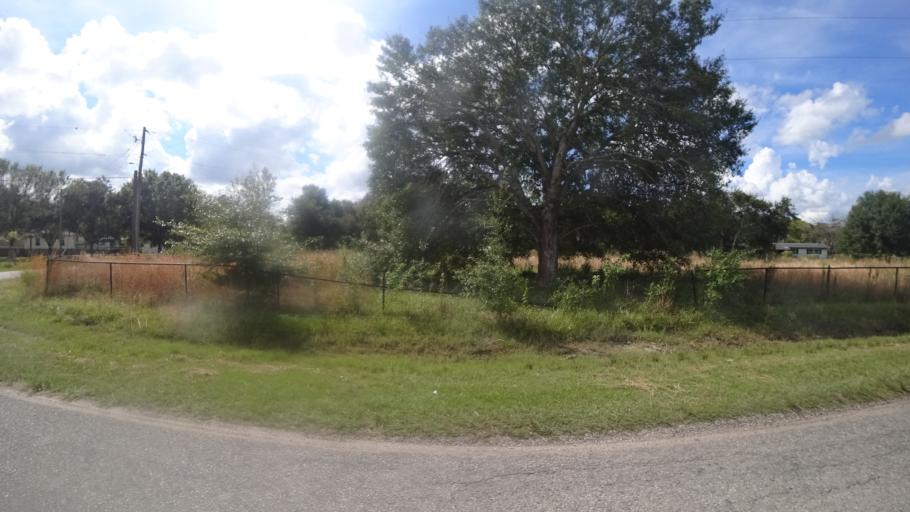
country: US
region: Florida
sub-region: Hillsborough County
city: Sun City Center
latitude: 27.6520
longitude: -82.3634
